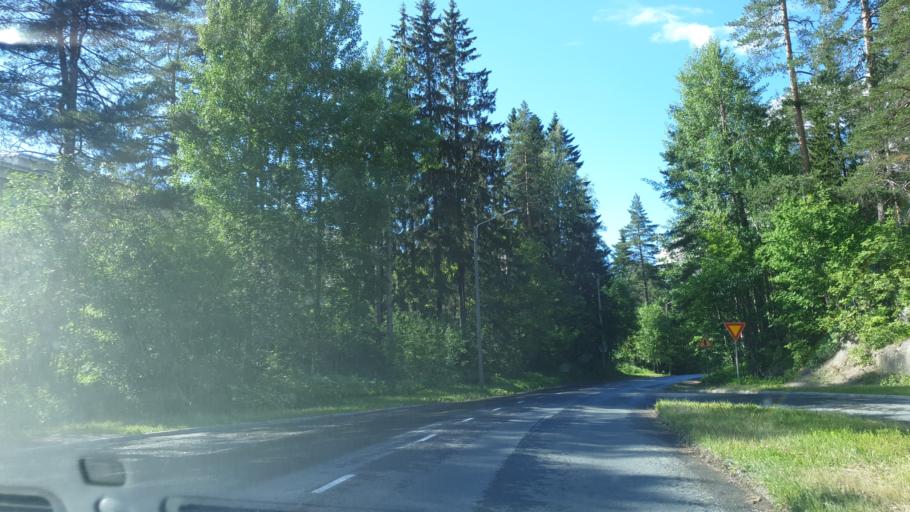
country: FI
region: Northern Savo
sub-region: Kuopio
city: Kuopio
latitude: 62.9062
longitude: 27.6483
